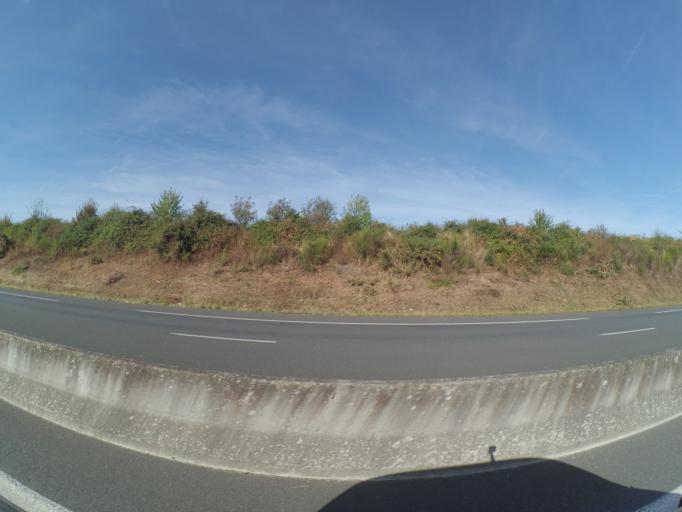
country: FR
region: Pays de la Loire
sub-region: Departement de Maine-et-Loire
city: Vezins
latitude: 47.1195
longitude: -0.7267
